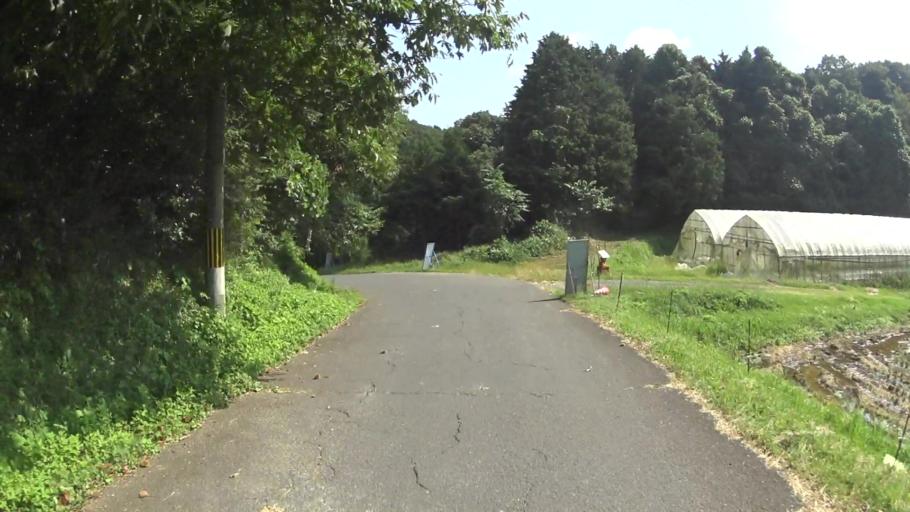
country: JP
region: Kyoto
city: Miyazu
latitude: 35.6749
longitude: 135.2410
